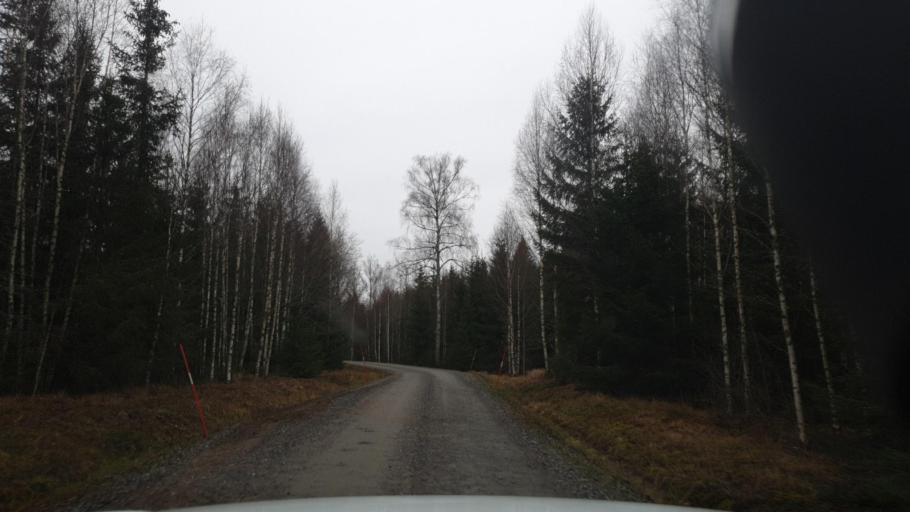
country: SE
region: Vaermland
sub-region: Karlstads Kommun
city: Edsvalla
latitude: 59.4656
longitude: 13.1227
